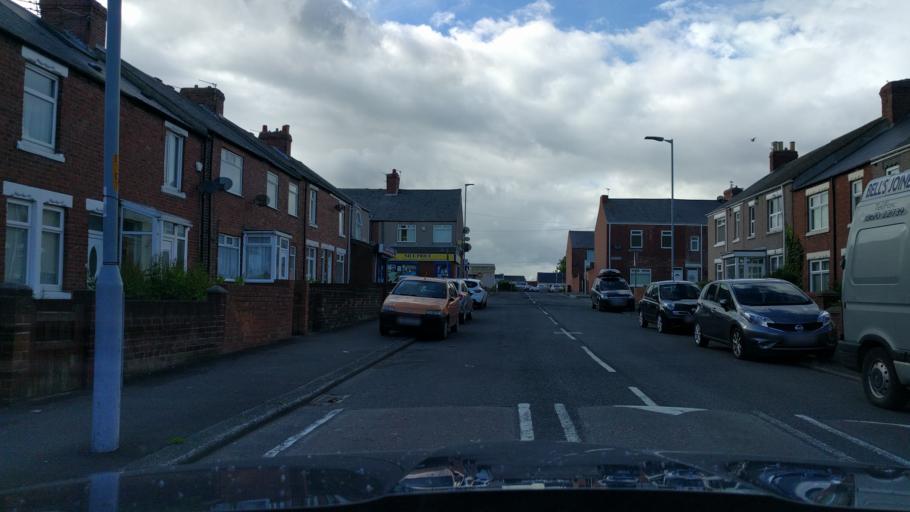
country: GB
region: England
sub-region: Northumberland
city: Lynemouth
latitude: 55.1842
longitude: -1.5580
